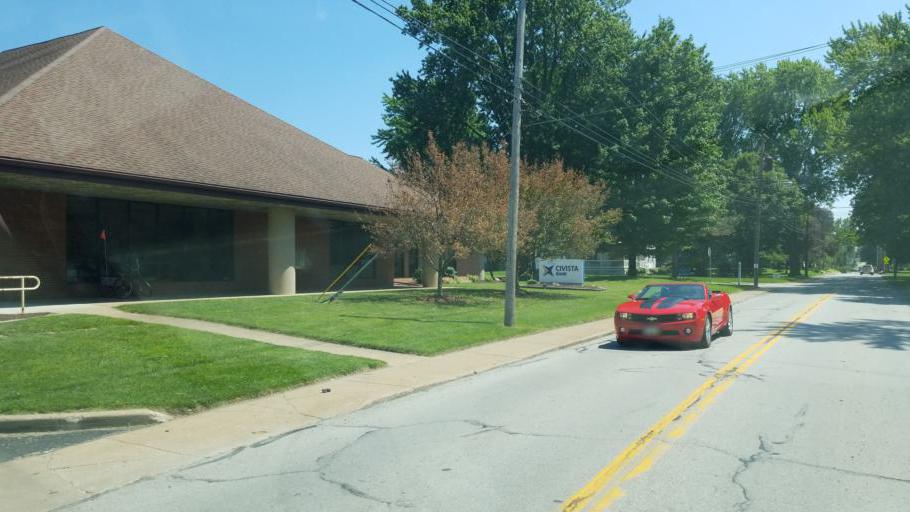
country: US
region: Ohio
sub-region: Erie County
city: Sandusky
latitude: 41.3982
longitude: -82.8081
